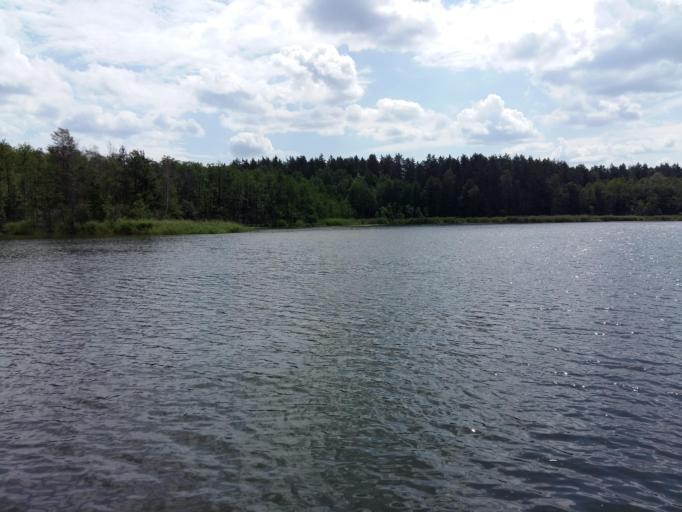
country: LT
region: Alytaus apskritis
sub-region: Alytaus rajonas
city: Daugai
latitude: 54.1758
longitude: 24.2241
